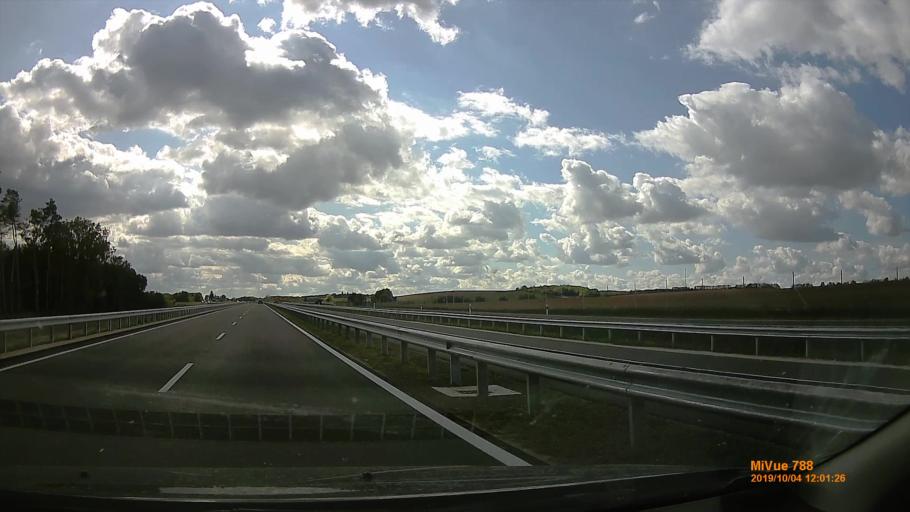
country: HU
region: Somogy
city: Karad
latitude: 46.6125
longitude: 17.7976
